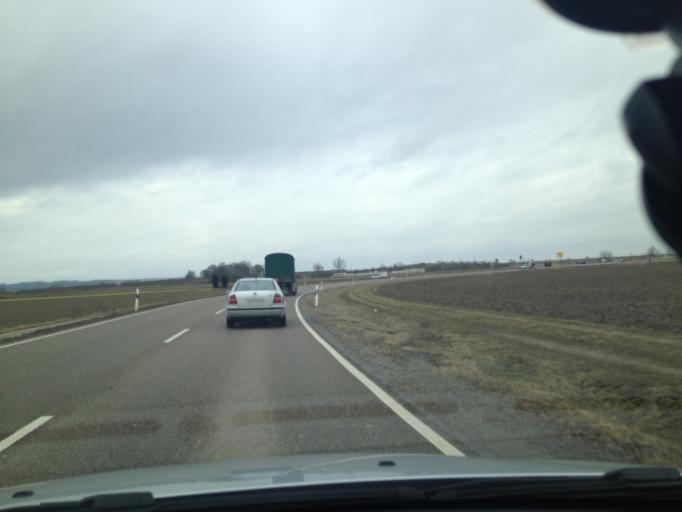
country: DE
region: Bavaria
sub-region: Swabia
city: Gersthofen
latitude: 48.4107
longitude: 10.8382
